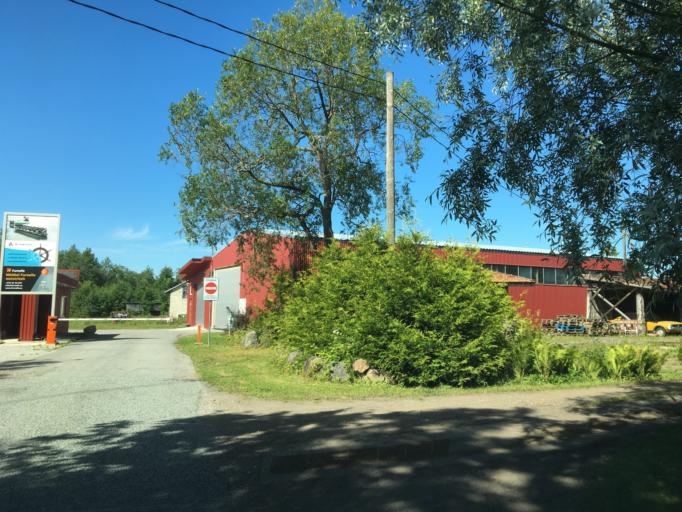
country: EE
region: Harju
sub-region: Saue linn
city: Saue
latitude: 59.2744
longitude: 24.5067
